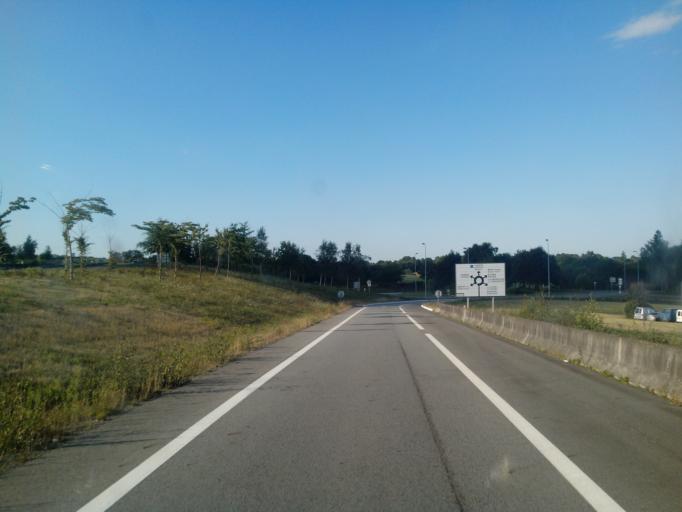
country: FR
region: Brittany
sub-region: Departement du Morbihan
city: Pontivy
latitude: 48.0672
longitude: -2.9424
